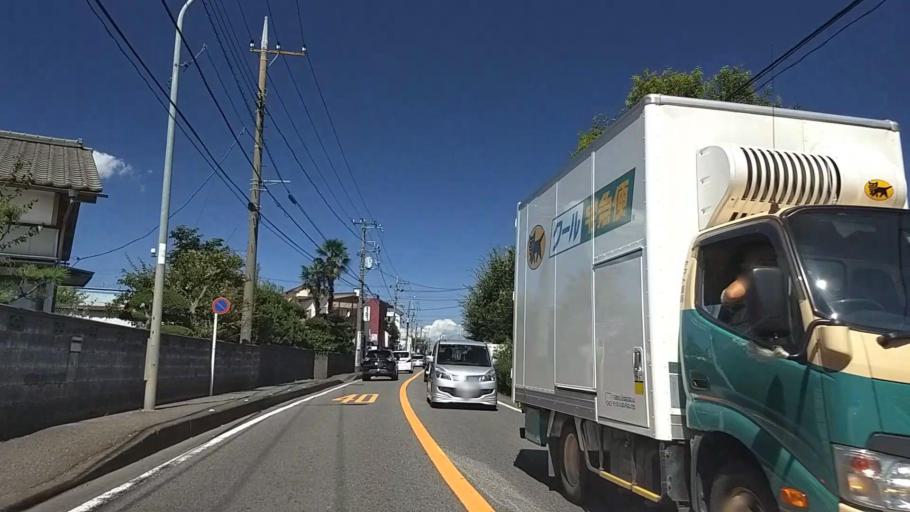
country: JP
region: Kanagawa
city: Zama
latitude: 35.5583
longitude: 139.3275
